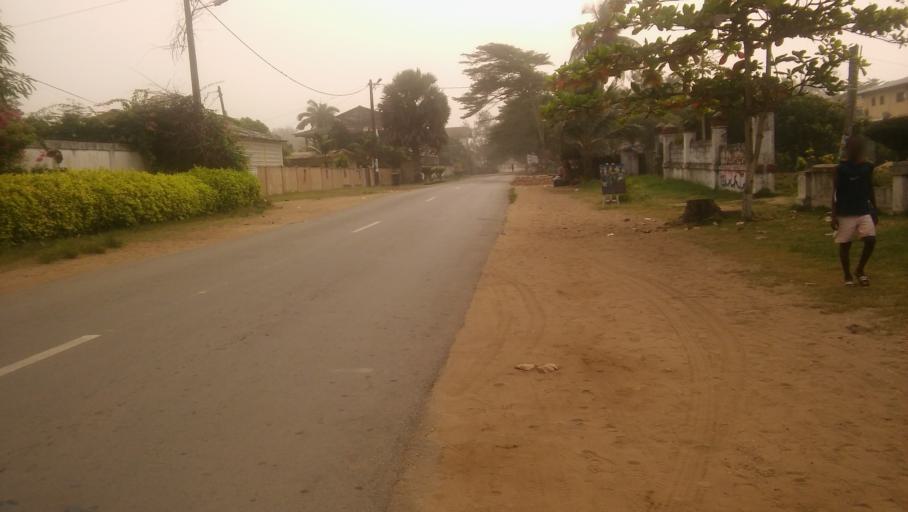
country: CI
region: Sud-Comoe
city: Grand-Bassam
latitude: 5.1956
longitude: -3.7364
